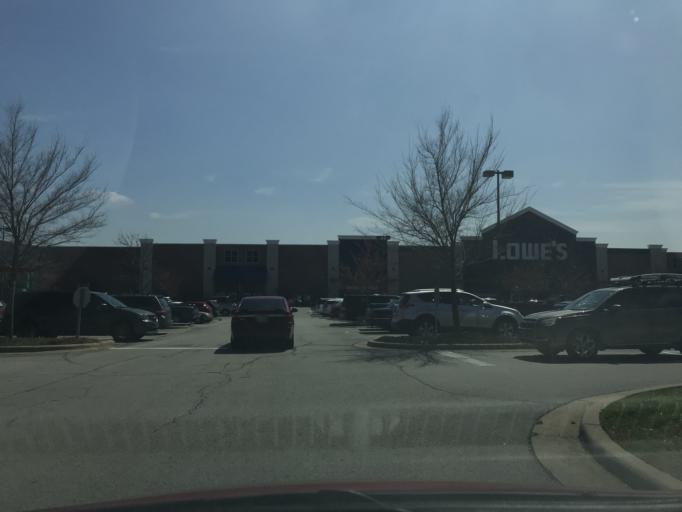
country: US
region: Kentucky
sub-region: Jefferson County
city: West Buechel
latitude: 38.2018
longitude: -85.6659
